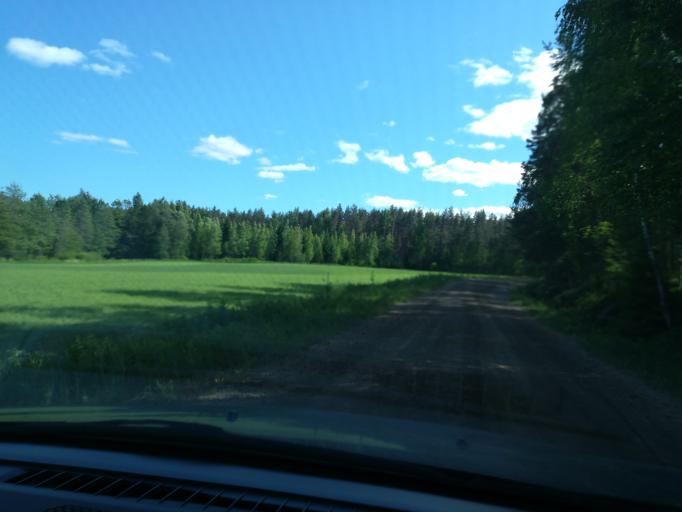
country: FI
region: Southern Savonia
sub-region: Mikkeli
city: Puumala
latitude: 61.6577
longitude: 28.1270
